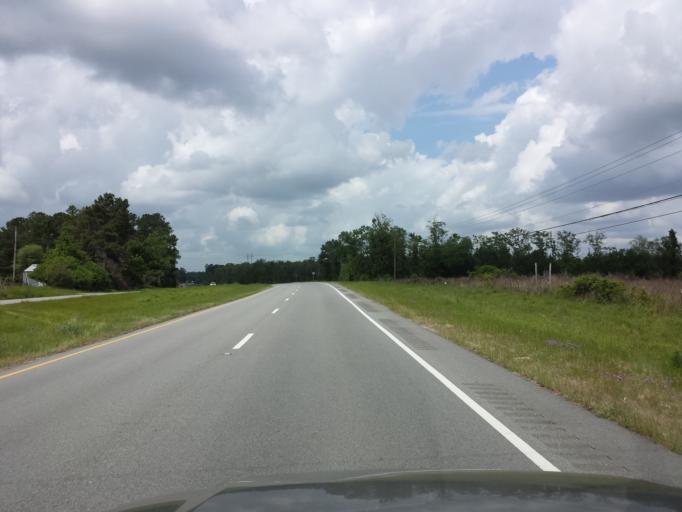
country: US
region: Georgia
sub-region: Lowndes County
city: Valdosta
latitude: 30.7208
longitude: -83.2161
